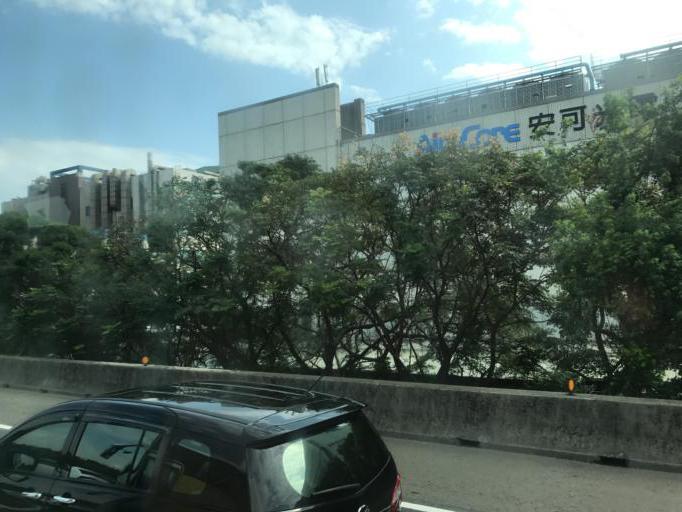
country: TW
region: Taiwan
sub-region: Hsinchu
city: Zhubei
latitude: 24.8769
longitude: 121.0372
